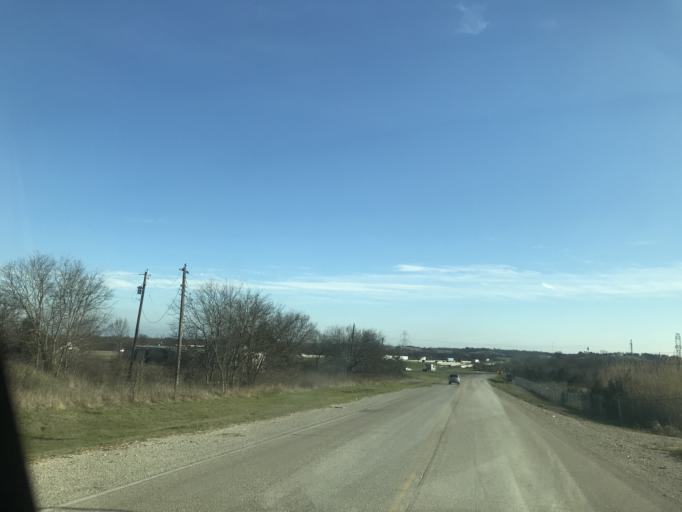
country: US
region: Texas
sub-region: Ellis County
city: Ferris
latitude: 32.5633
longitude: -96.6674
